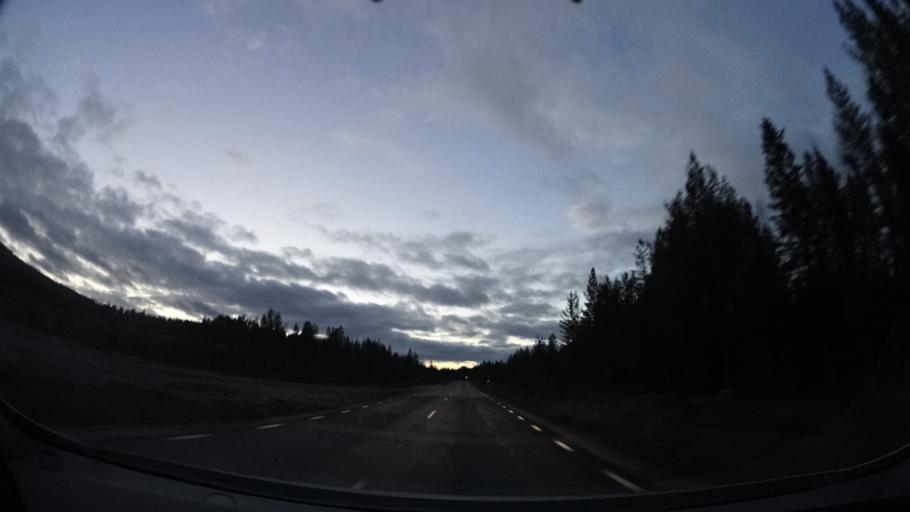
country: SE
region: Vaesterbotten
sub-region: Asele Kommun
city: Asele
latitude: 64.2071
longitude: 16.9844
